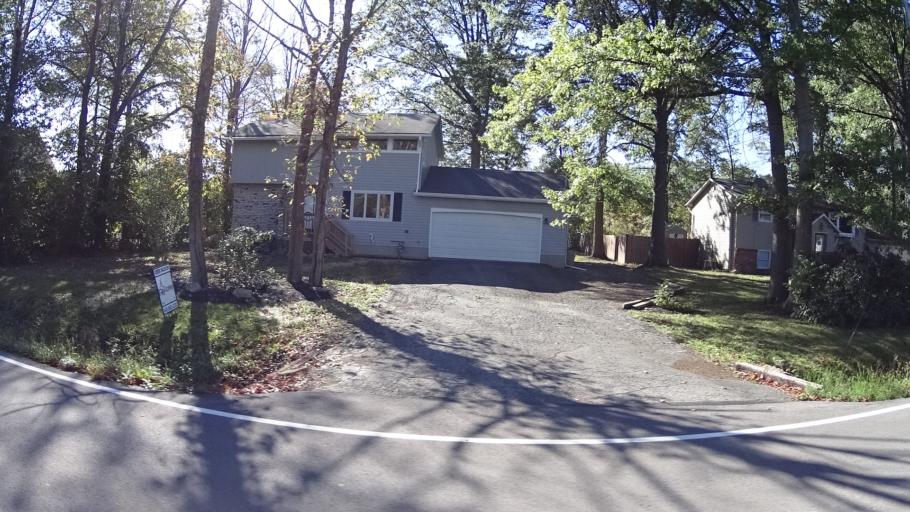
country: US
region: Ohio
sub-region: Lorain County
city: Amherst
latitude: 41.4118
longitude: -82.2438
